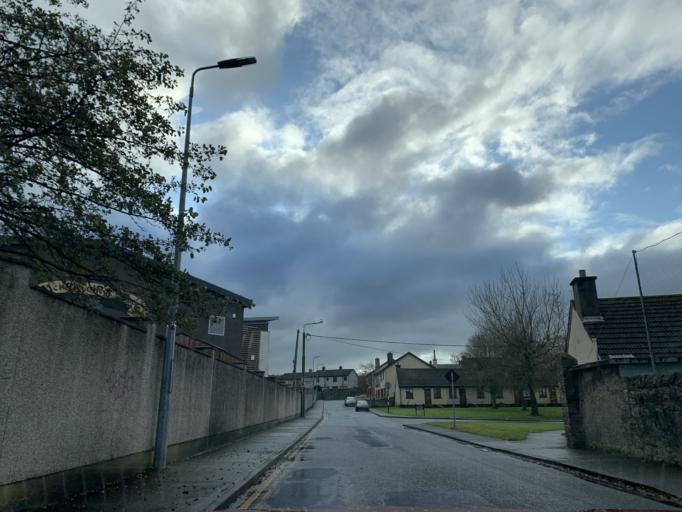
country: IE
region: Connaught
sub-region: Sligo
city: Sligo
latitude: 54.2674
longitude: -8.4689
